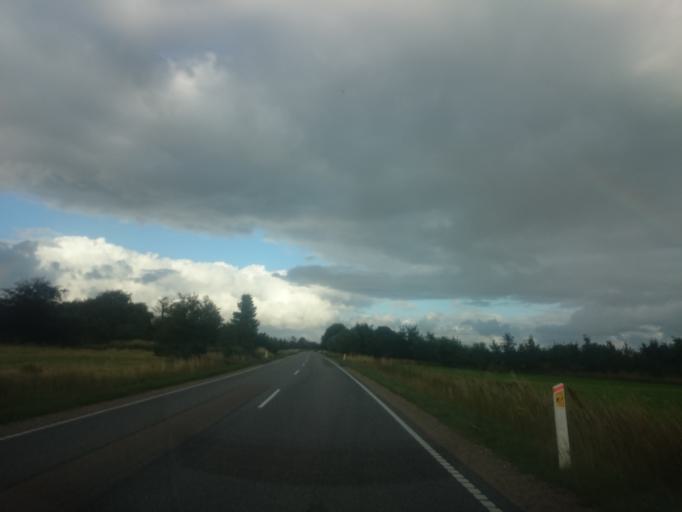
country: DK
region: South Denmark
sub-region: Varde Kommune
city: Olgod
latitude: 55.6657
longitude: 8.7433
